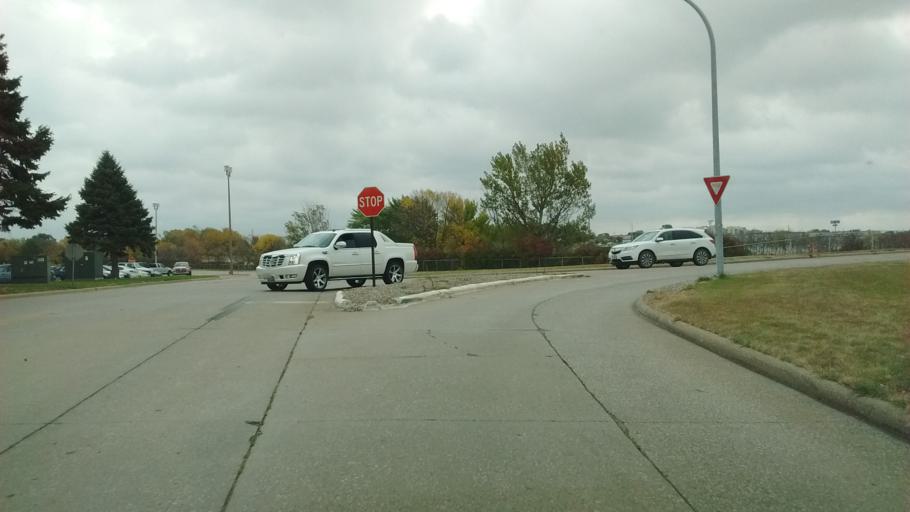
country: US
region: Iowa
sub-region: Woodbury County
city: Sergeant Bluff
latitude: 42.4445
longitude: -96.3533
